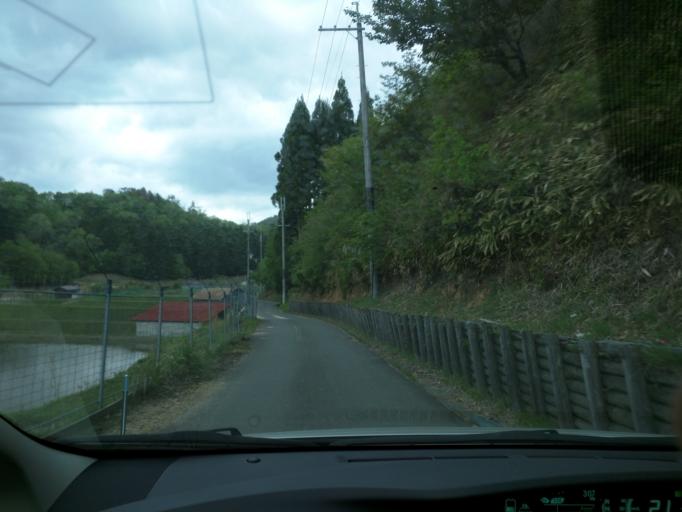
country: JP
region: Mie
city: Ueno-ebisumachi
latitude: 34.8270
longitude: 135.9947
